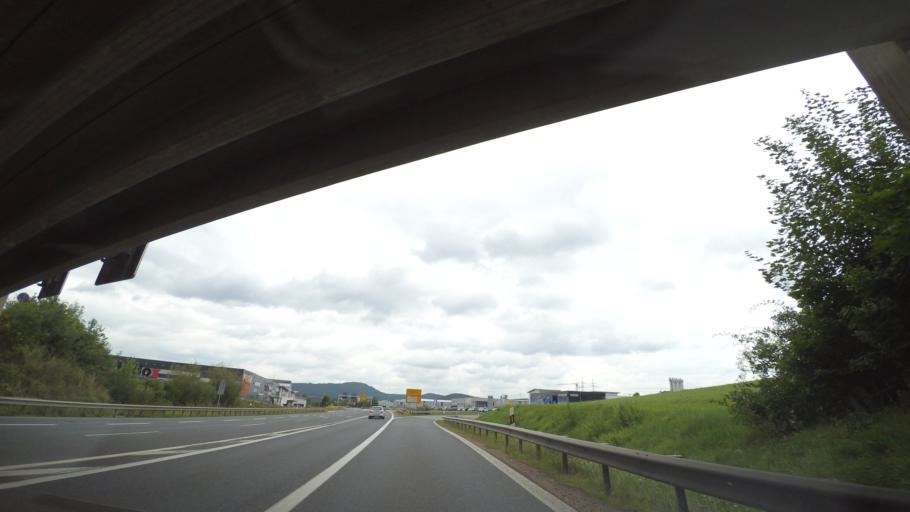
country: DE
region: Bavaria
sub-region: Upper Palatinate
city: Cham
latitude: 49.2004
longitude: 12.6602
